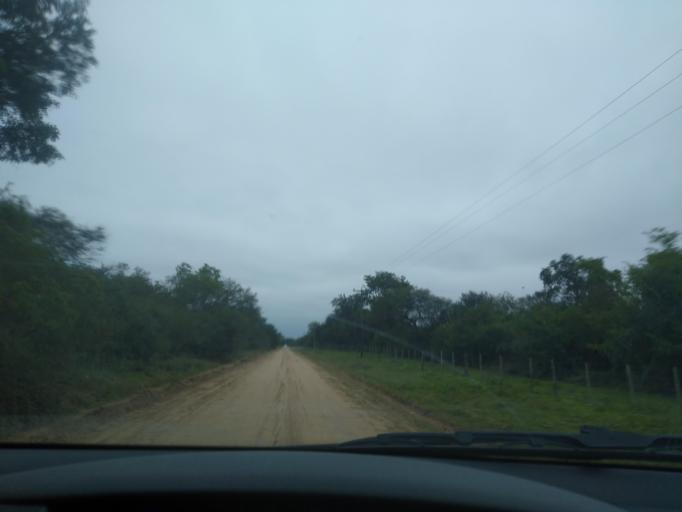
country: AR
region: Chaco
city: Colonia Benitez
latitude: -27.3521
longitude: -58.9685
